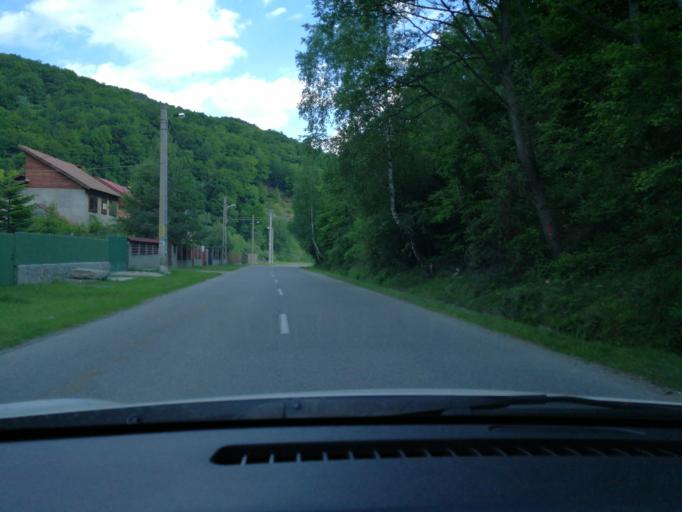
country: RO
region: Prahova
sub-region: Comuna Sotrile
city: Sotrile
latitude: 45.2421
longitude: 25.7320
